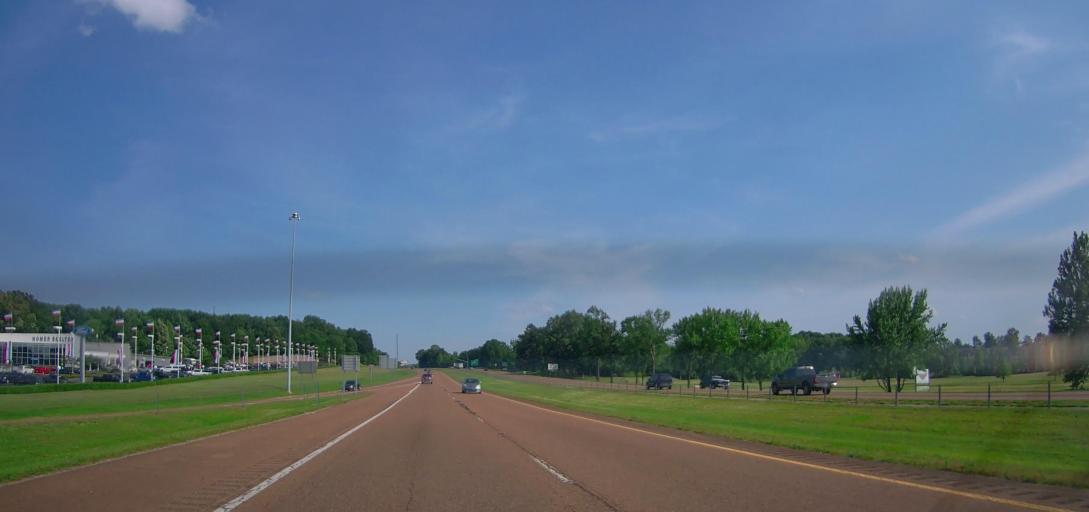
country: US
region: Mississippi
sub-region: De Soto County
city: Olive Branch
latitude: 34.9606
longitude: -89.8511
